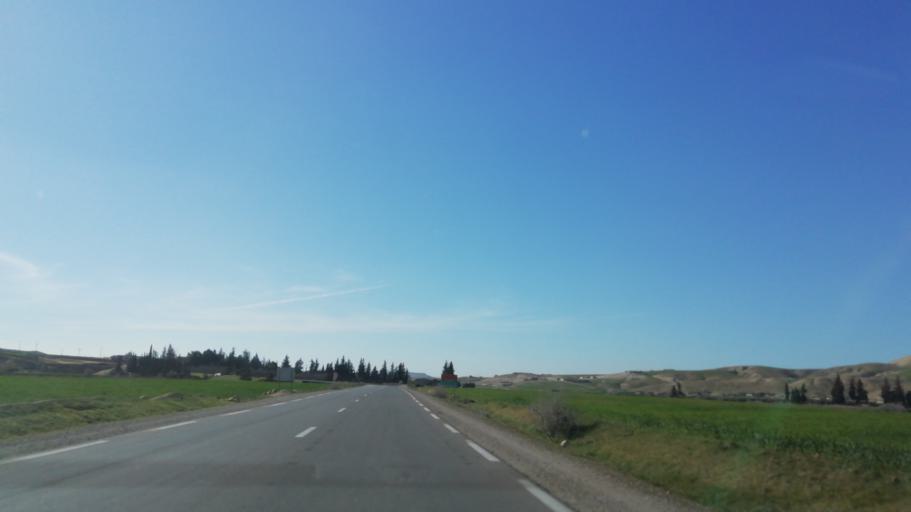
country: DZ
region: Mascara
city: Oued el Abtal
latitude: 35.4569
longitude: 0.7580
